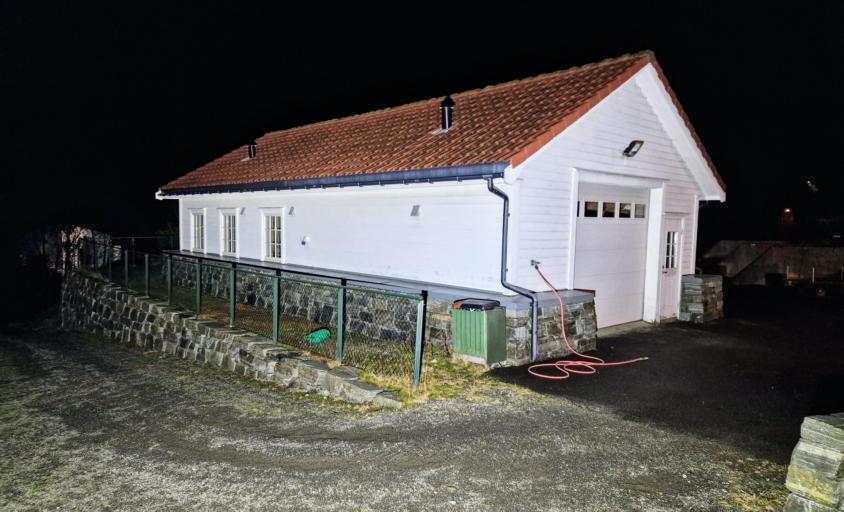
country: NO
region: Rogaland
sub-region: Finnoy
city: Judaberg
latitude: 59.3498
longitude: 5.8014
